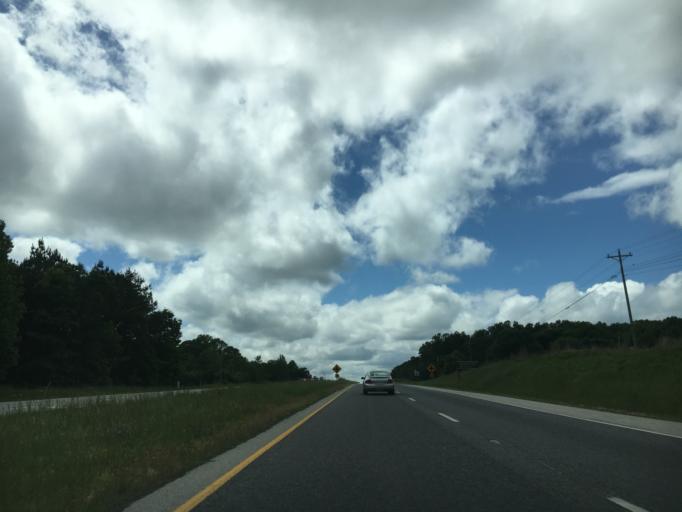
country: US
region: Virginia
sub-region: Mecklenburg County
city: Boydton
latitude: 36.6716
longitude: -78.2830
